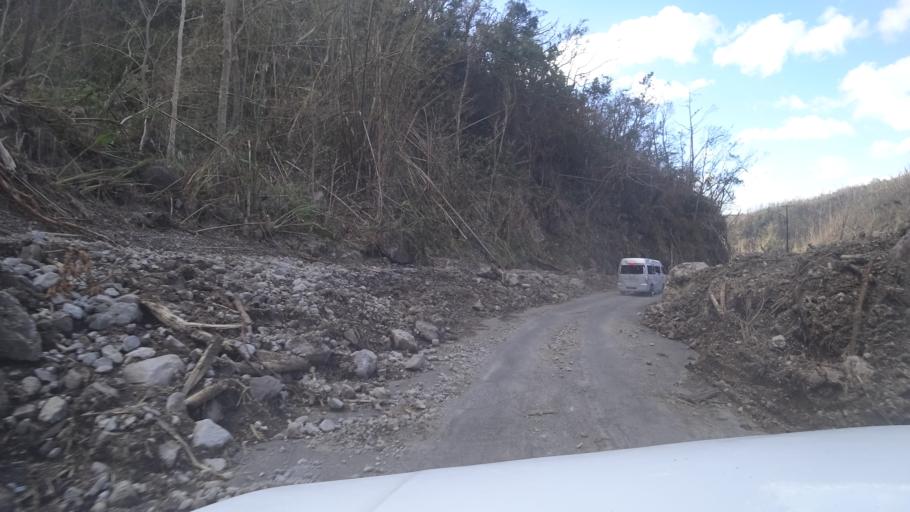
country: DM
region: Saint Luke
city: Pointe Michel
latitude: 15.2707
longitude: -61.3531
